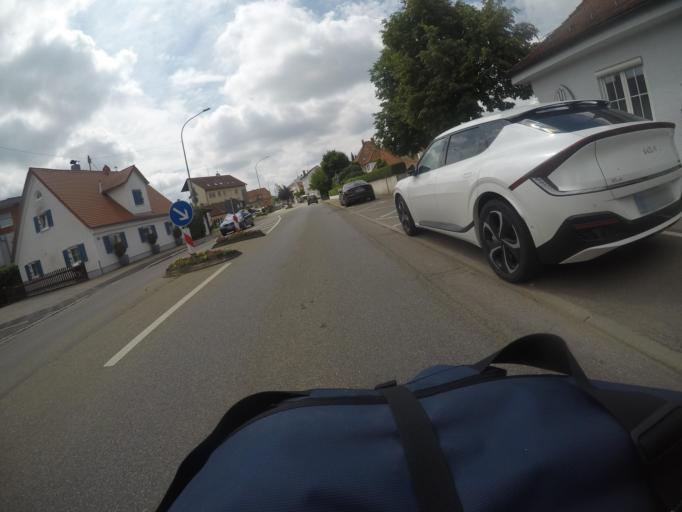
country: DE
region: Bavaria
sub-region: Swabia
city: Vohringen
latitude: 48.2803
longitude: 10.0777
